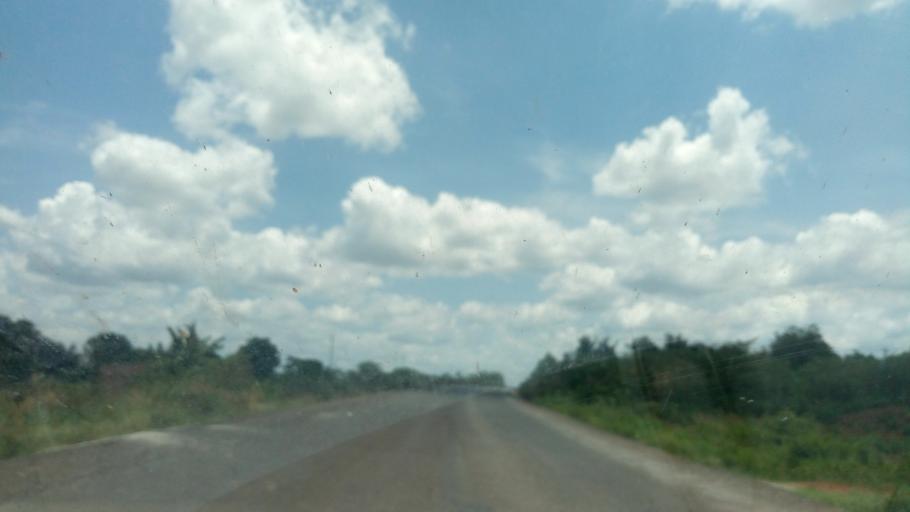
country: UG
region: Western Region
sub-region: Kiryandongo District
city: Kiryandongo
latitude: 1.7905
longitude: 31.9423
